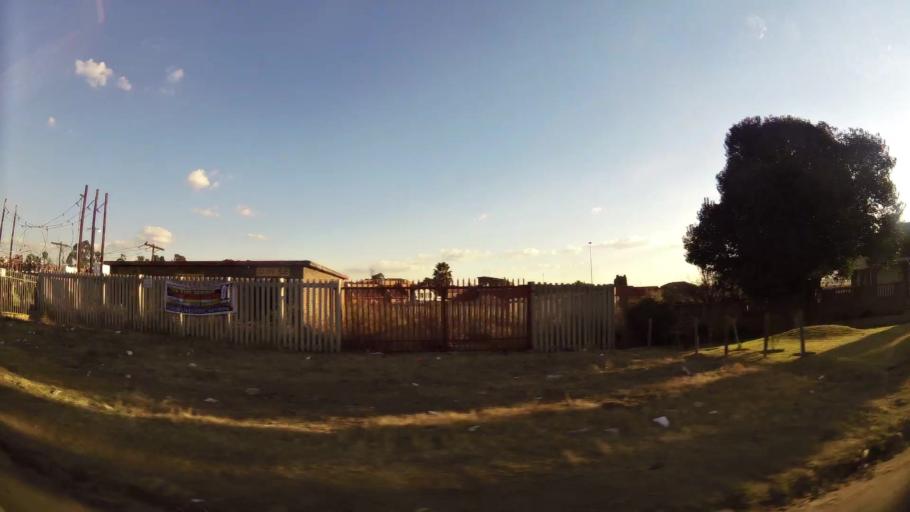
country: ZA
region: Mpumalanga
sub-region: Nkangala District Municipality
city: Witbank
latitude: -25.8794
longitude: 29.1833
